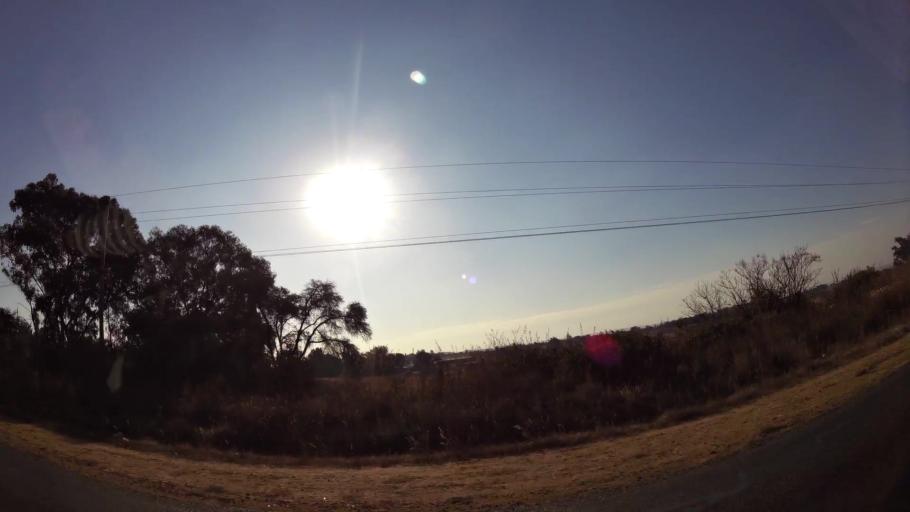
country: ZA
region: Gauteng
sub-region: West Rand District Municipality
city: Muldersdriseloop
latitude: -26.0158
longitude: 27.8863
